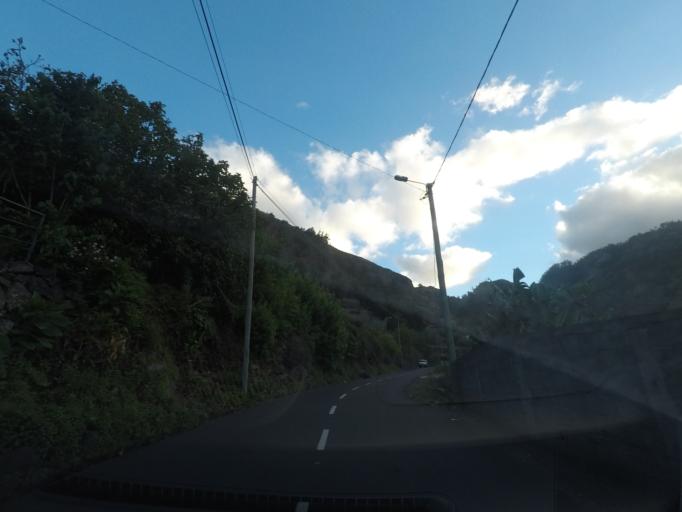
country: PT
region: Madeira
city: Ponta do Sol
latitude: 32.6906
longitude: -17.0746
